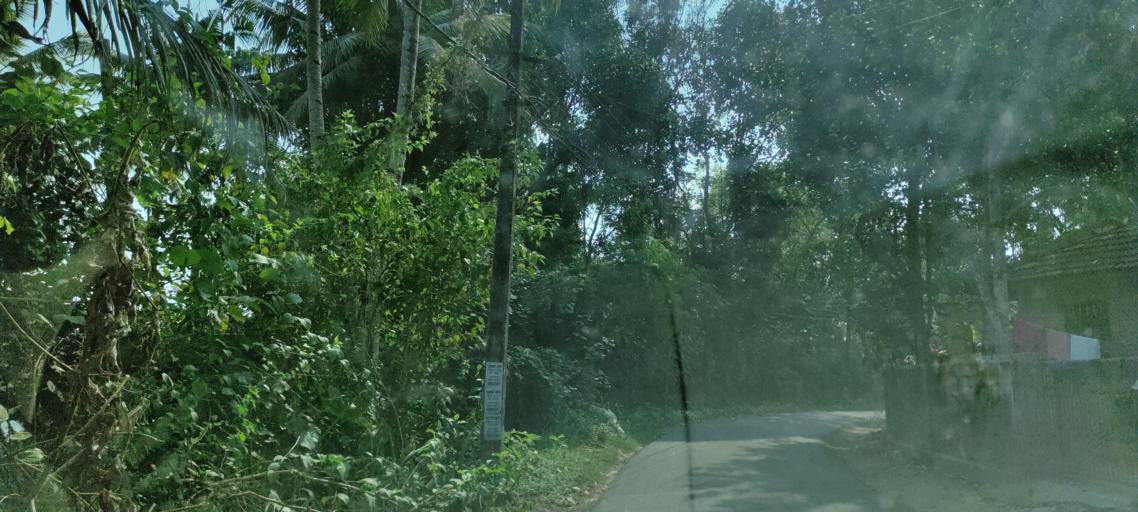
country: IN
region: Kerala
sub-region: Pattanamtitta
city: Tiruvalla
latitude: 9.3447
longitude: 76.5421
